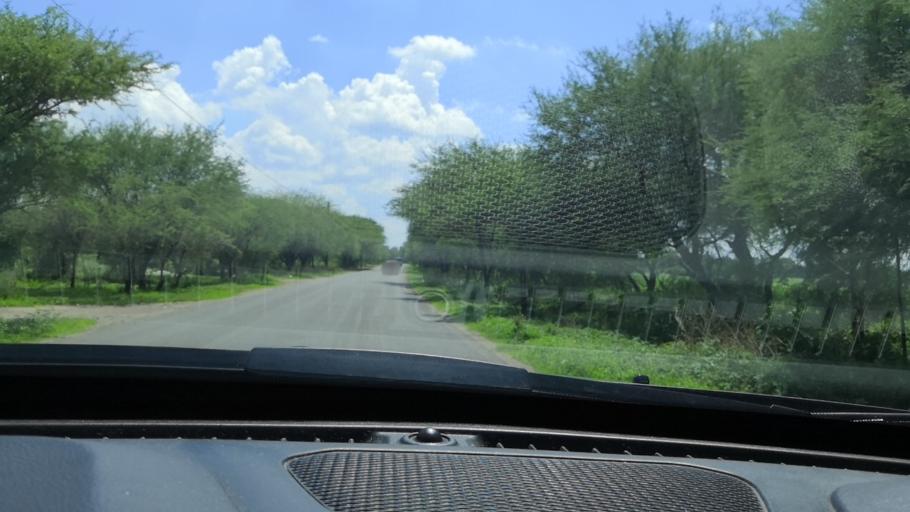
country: MX
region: Guanajuato
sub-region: Leon
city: Plan Guanajuato (La Sandia)
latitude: 20.9387
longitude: -101.6344
